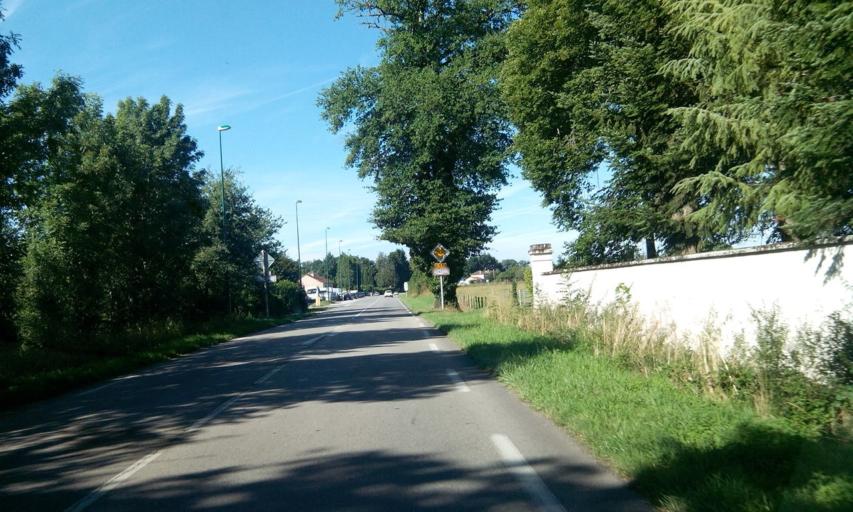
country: FR
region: Limousin
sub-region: Departement de la Haute-Vienne
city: Panazol
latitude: 45.8385
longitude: 1.3232
